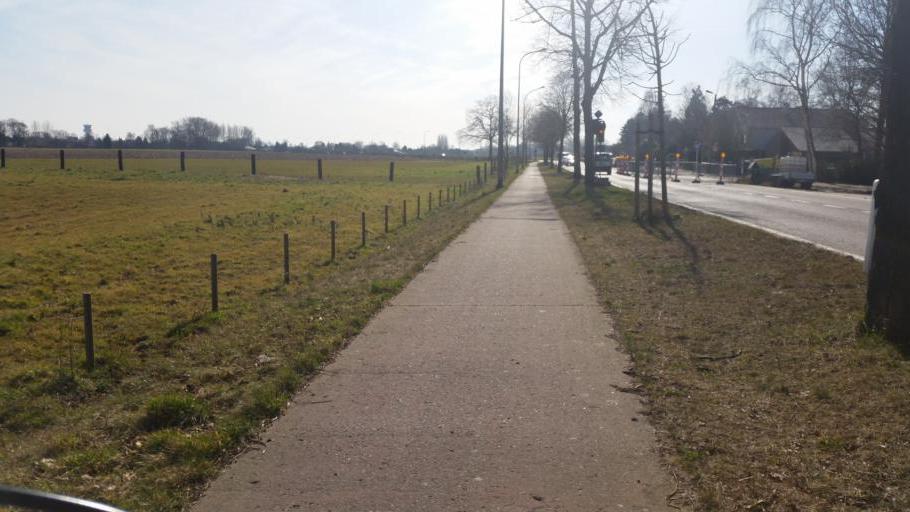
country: BE
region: Flanders
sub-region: Provincie Vlaams-Brabant
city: Steenokkerzeel
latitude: 50.9285
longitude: 4.4979
